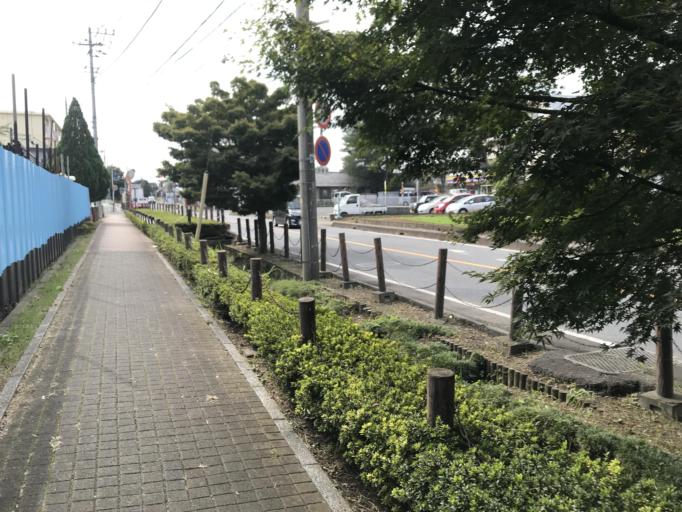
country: JP
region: Tokyo
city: Tanashicho
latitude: 35.7706
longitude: 139.5335
